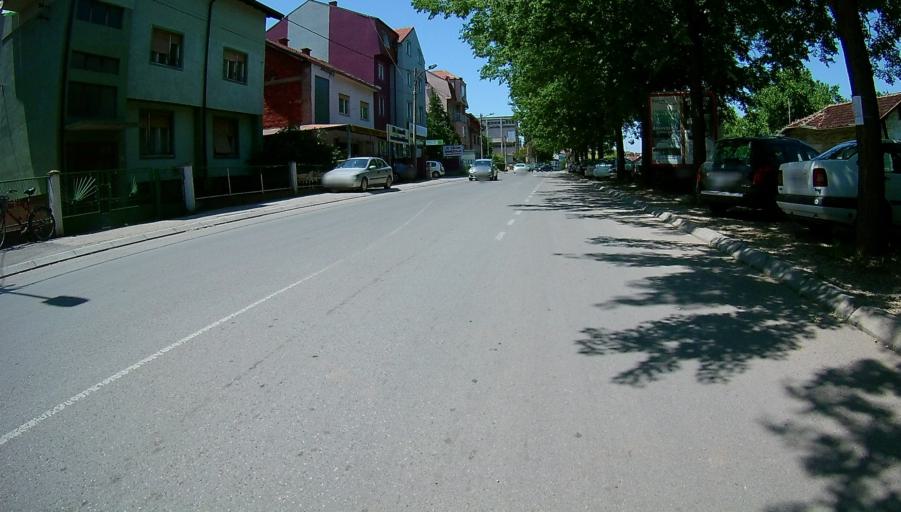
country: RS
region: Central Serbia
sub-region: Nisavski Okrug
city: Nis
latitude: 43.3126
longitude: 21.8952
